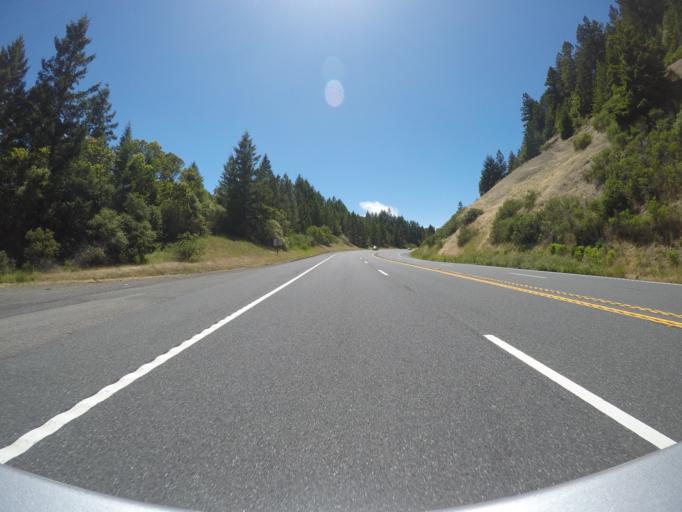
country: US
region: California
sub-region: Mendocino County
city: Laytonville
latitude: 39.8266
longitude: -123.6678
